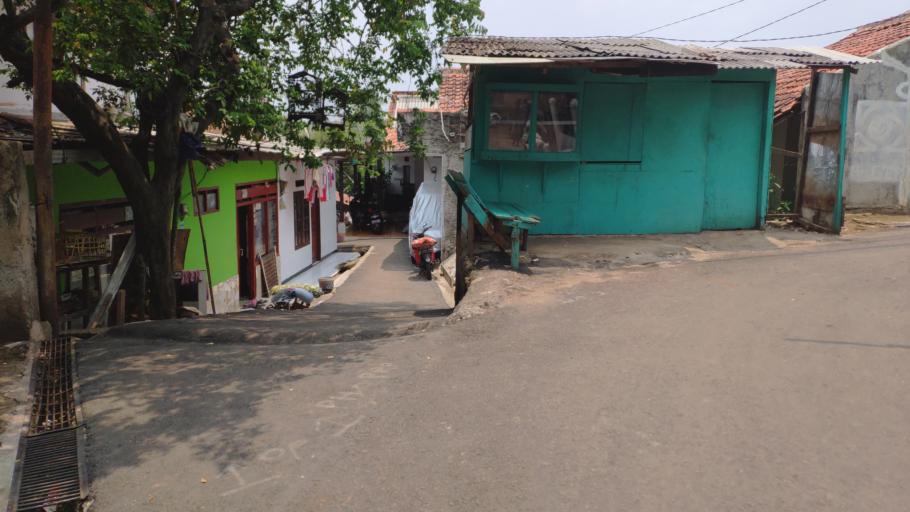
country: ID
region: West Java
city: Depok
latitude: -6.3470
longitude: 106.8054
